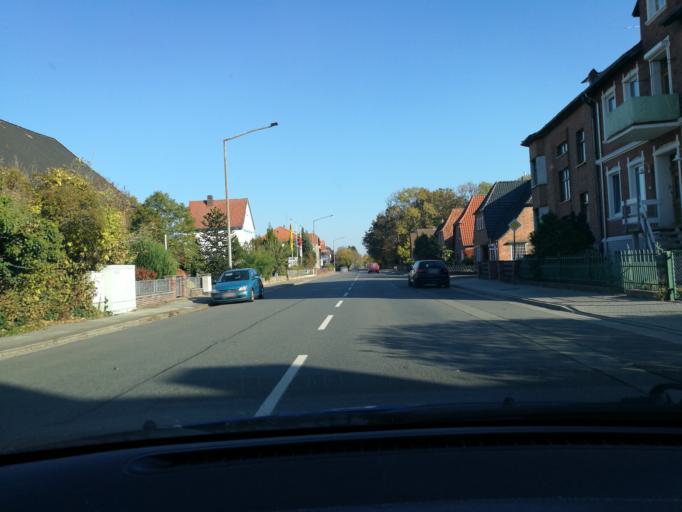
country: DE
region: Lower Saxony
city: Dannenberg
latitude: 53.1030
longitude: 11.1121
